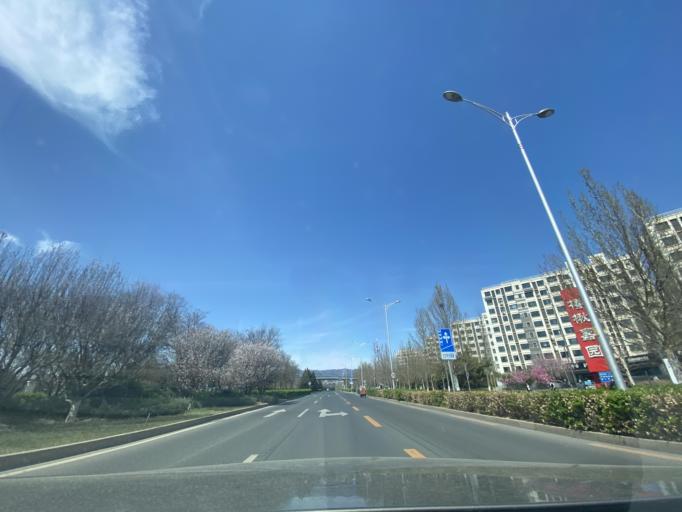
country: CN
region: Beijing
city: Sijiqing
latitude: 39.9343
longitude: 116.2454
